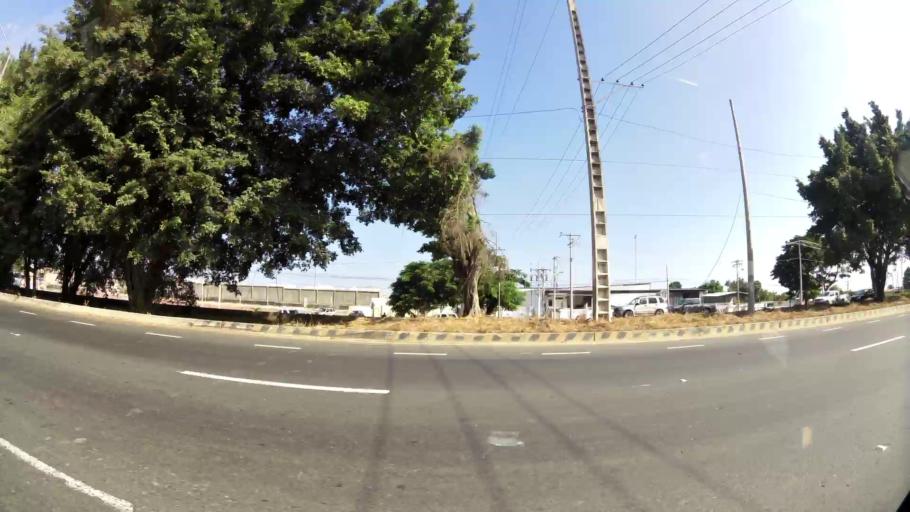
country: EC
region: Guayas
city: Santa Lucia
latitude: -2.1841
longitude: -79.9782
